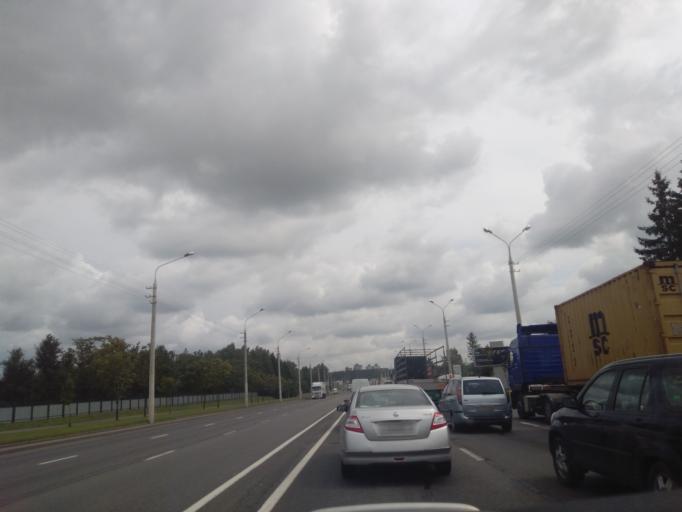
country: BY
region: Minsk
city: Lyeskawka
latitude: 53.9517
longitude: 27.7088
